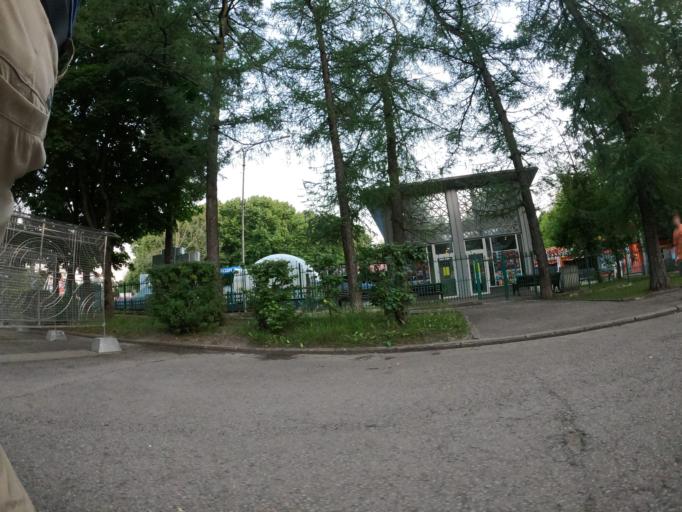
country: RU
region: Moscow
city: Sokol'niki
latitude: 55.7945
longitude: 37.6716
